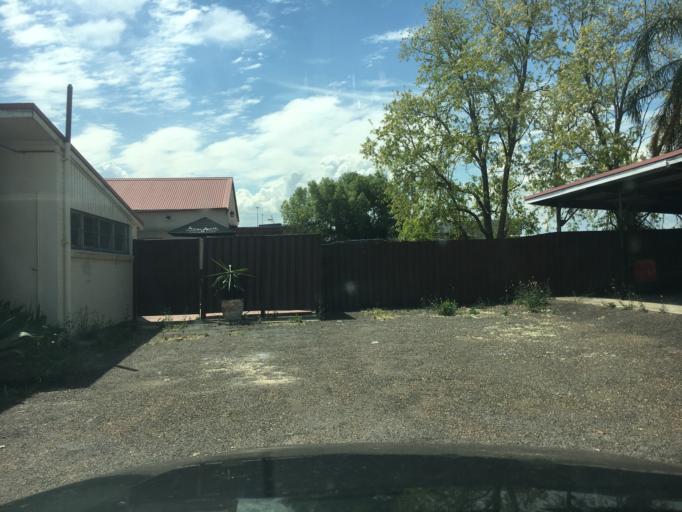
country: AU
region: New South Wales
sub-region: Singleton
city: Singleton
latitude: -32.5680
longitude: 151.1651
